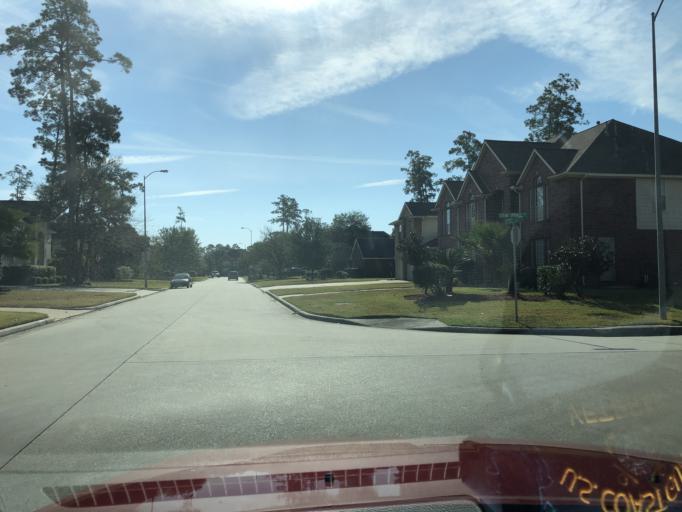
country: US
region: Texas
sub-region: Harris County
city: Tomball
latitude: 30.0269
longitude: -95.5606
